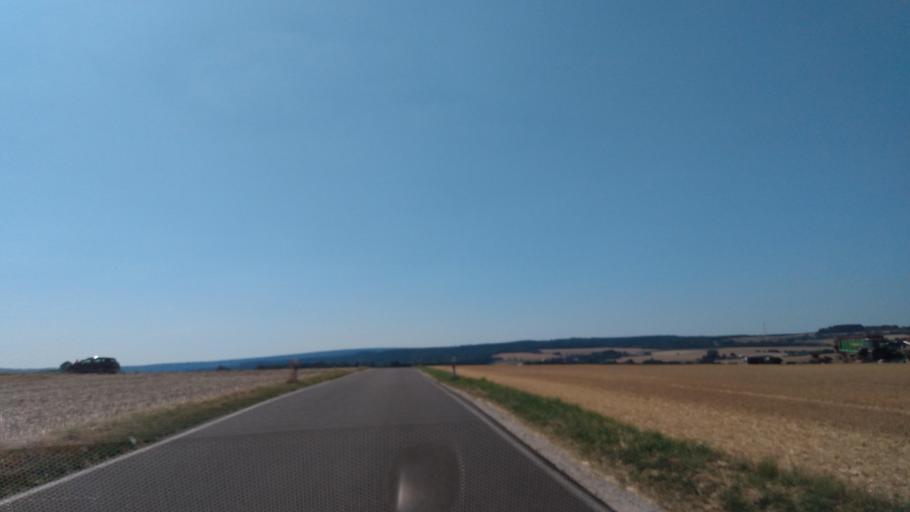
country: DE
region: Rheinland-Pfalz
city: Kleinich
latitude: 49.9139
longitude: 7.1848
